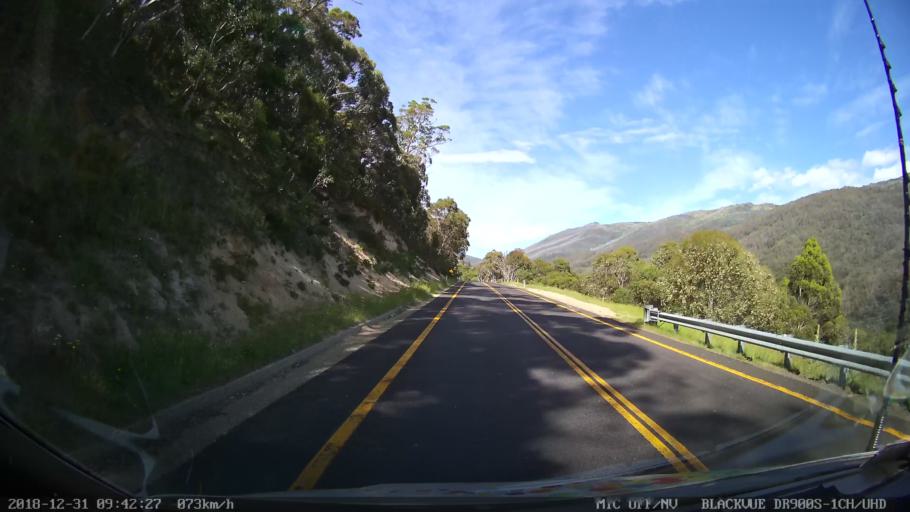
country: AU
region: New South Wales
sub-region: Snowy River
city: Jindabyne
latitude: -36.4965
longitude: 148.3227
